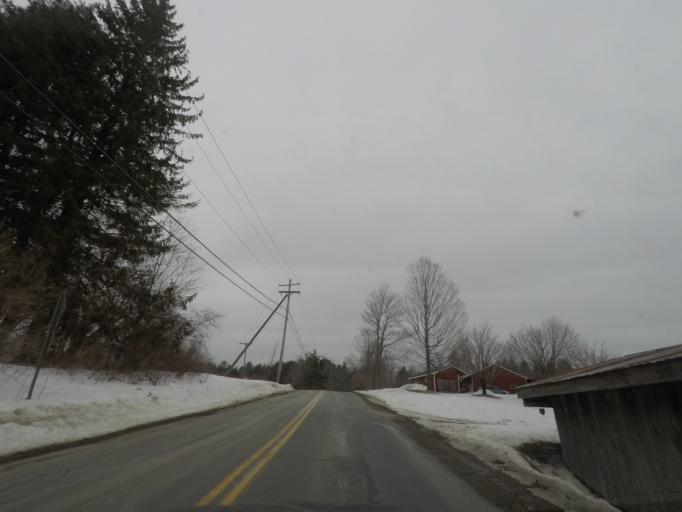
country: US
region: Massachusetts
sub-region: Berkshire County
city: Lanesborough
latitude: 42.5594
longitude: -73.3845
